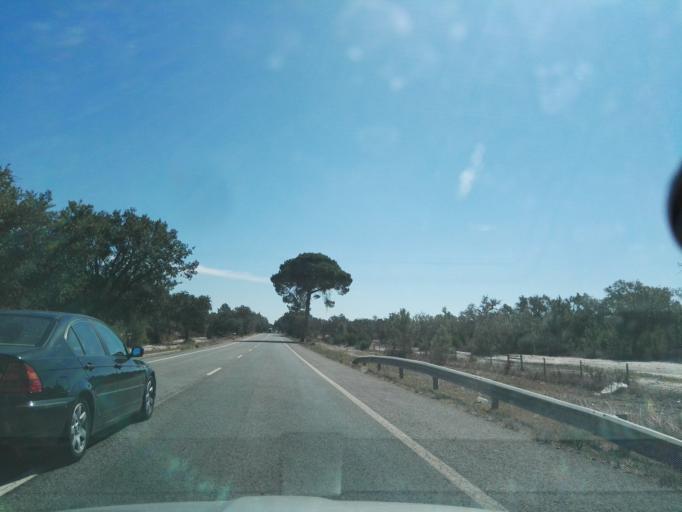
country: PT
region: Santarem
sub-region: Benavente
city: Poceirao
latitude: 38.8800
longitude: -8.8138
